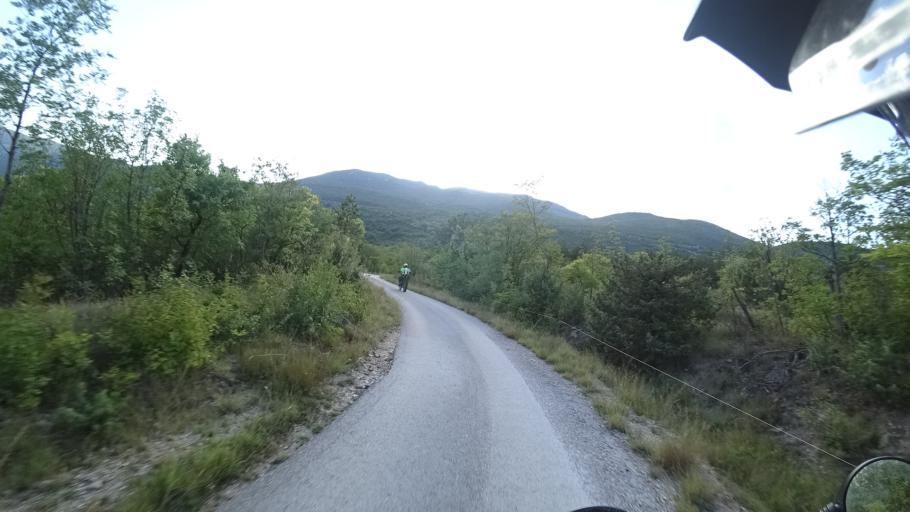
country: HR
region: Sibensko-Kniniska
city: Knin
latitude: 44.2008
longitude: 16.0625
